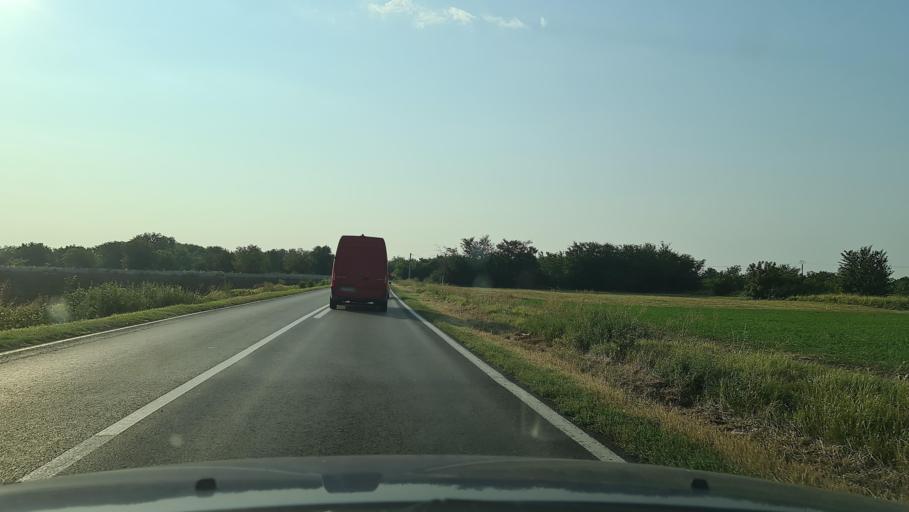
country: RO
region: Calarasi
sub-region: Comuna Dor Marunt
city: Dor Marunt
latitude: 44.4506
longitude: 26.9162
